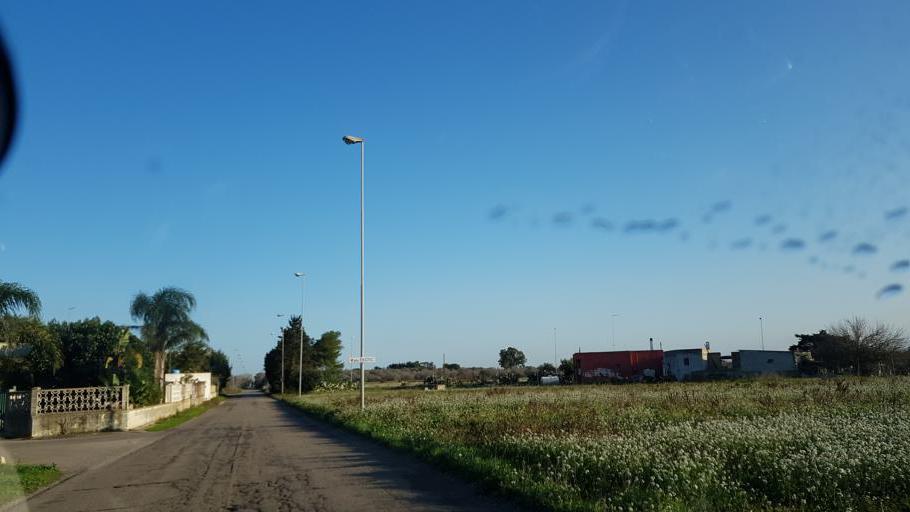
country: IT
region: Apulia
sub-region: Provincia di Brindisi
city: Torchiarolo
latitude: 40.5061
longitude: 18.0989
